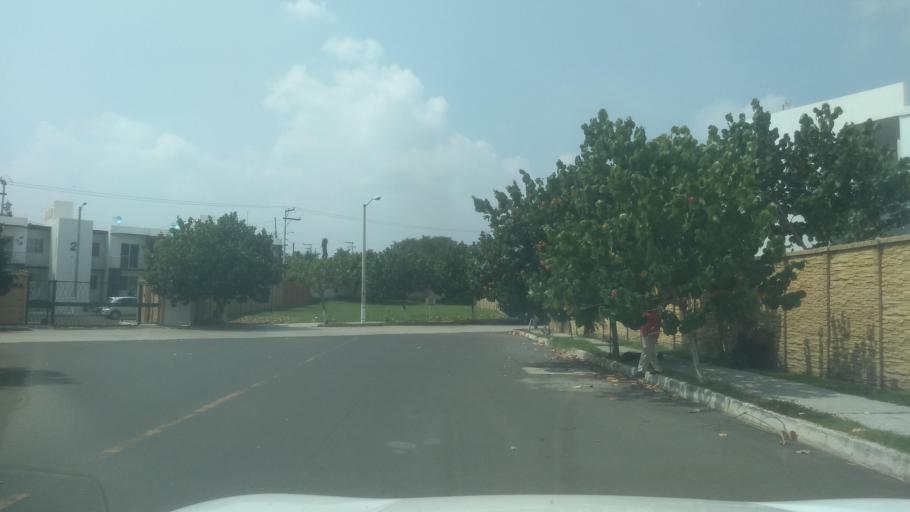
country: MX
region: Veracruz
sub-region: Veracruz
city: Las Amapolas
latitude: 19.1643
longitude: -96.1818
